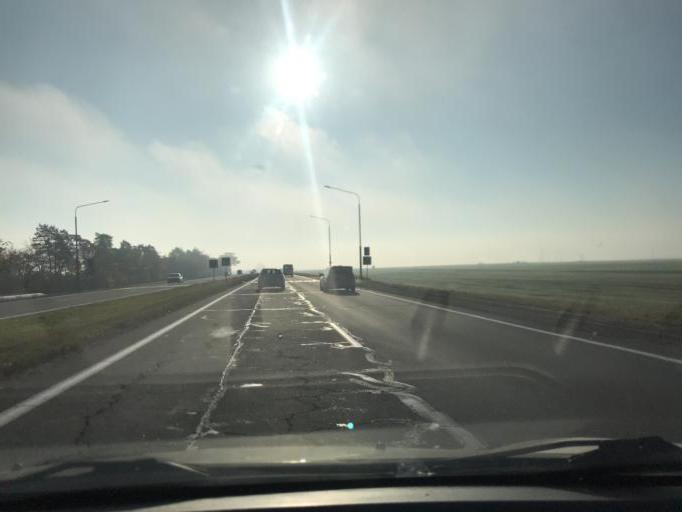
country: BY
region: Minsk
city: Dukora
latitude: 53.6976
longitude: 27.8907
